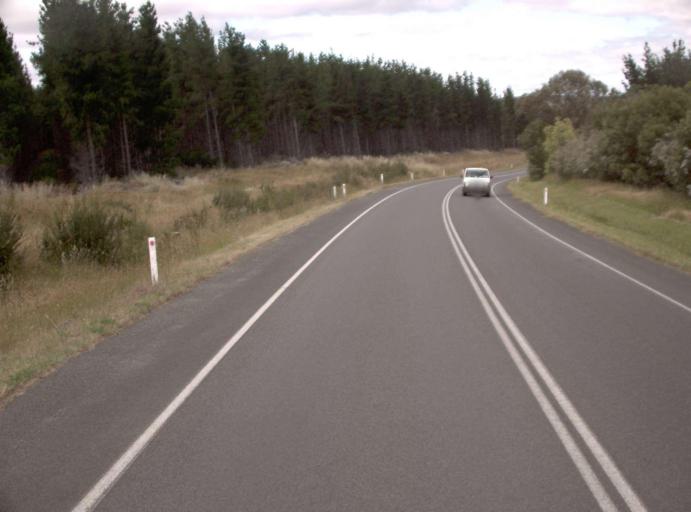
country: AU
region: Victoria
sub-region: Latrobe
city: Morwell
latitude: -38.1968
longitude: 146.4481
